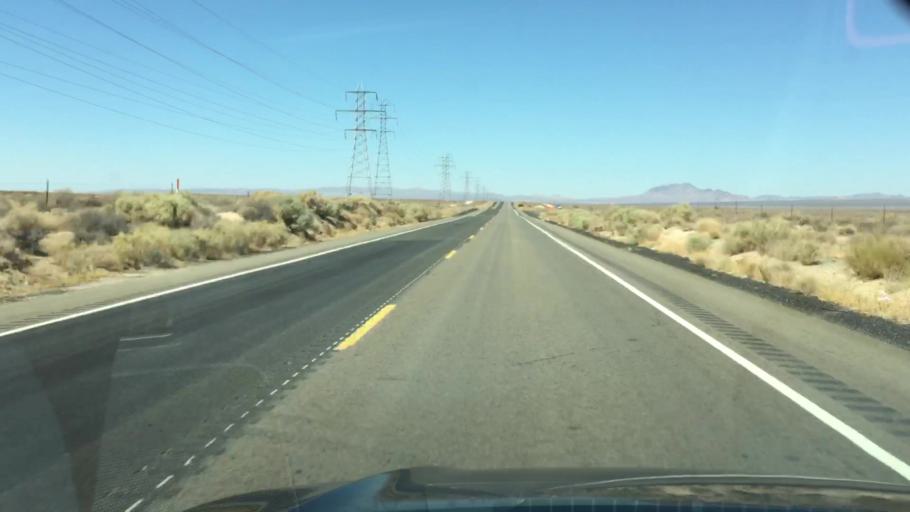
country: US
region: California
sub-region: Kern County
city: Boron
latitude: 35.0991
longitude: -117.5713
